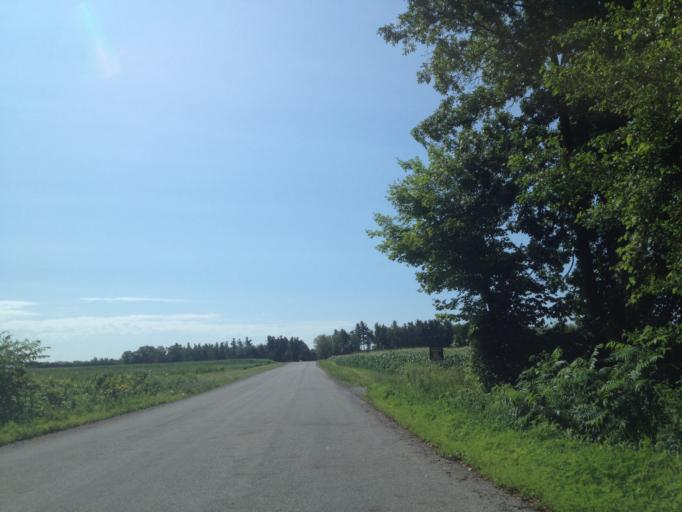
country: CA
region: Ontario
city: Norfolk County
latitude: 42.8314
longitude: -80.3894
